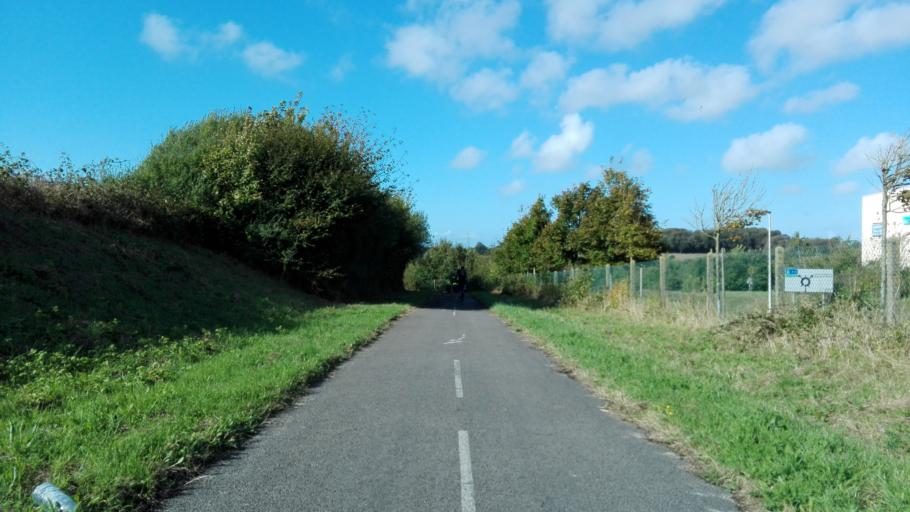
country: FR
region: Nord-Pas-de-Calais
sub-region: Departement du Pas-de-Calais
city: Baincthun
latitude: 50.7291
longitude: 1.6649
